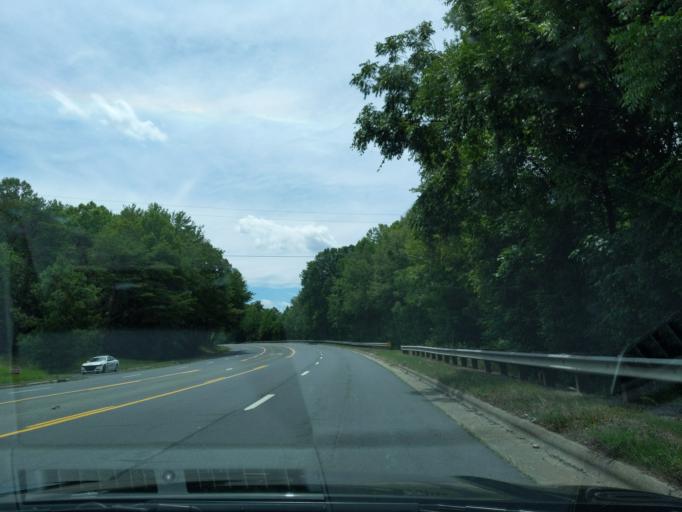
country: US
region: North Carolina
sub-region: Stanly County
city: Albemarle
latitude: 35.4418
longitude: -80.2216
